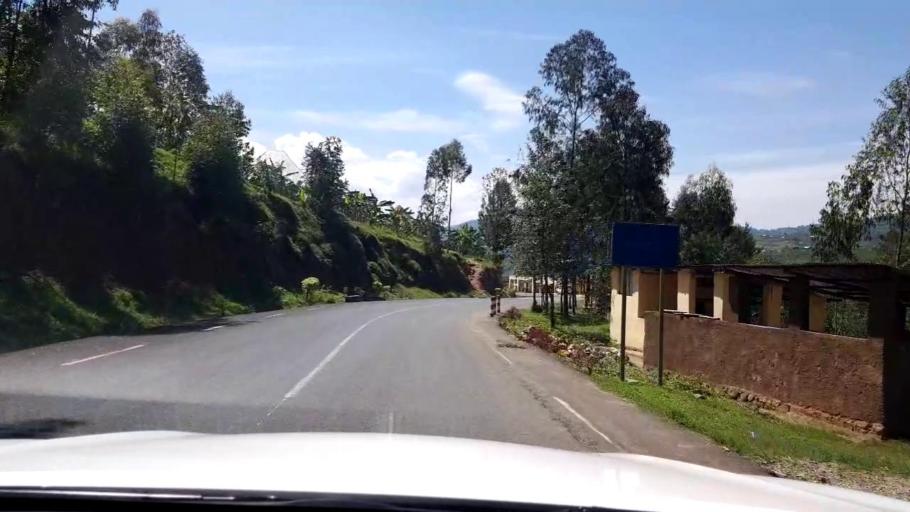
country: RW
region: Southern Province
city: Gitarama
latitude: -1.9166
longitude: 29.6295
